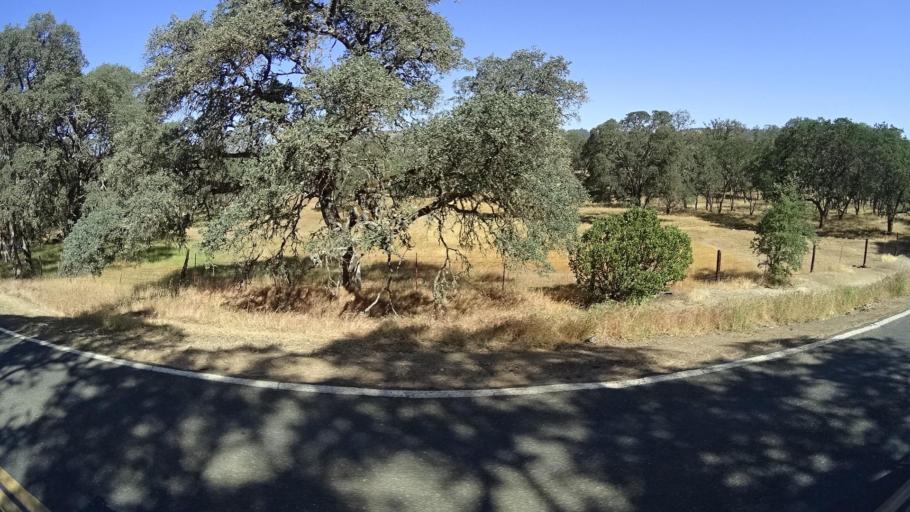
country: US
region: California
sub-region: Lake County
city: Clearlake Oaks
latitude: 39.0074
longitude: -122.6538
